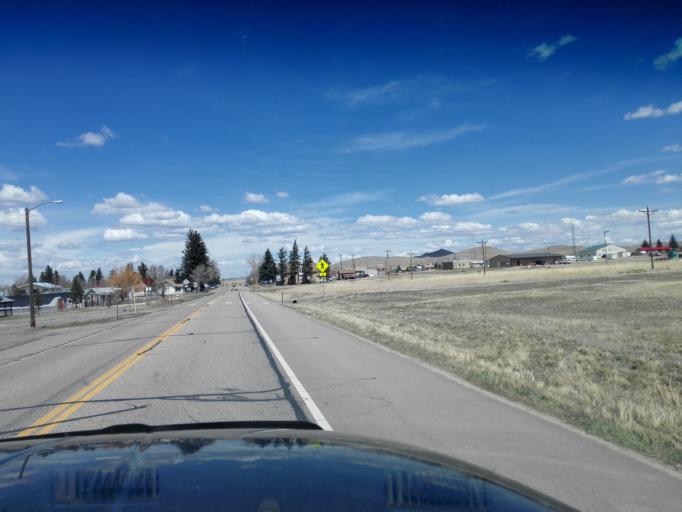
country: US
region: Colorado
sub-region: Custer County
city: Westcliffe
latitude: 38.1318
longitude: -105.4639
